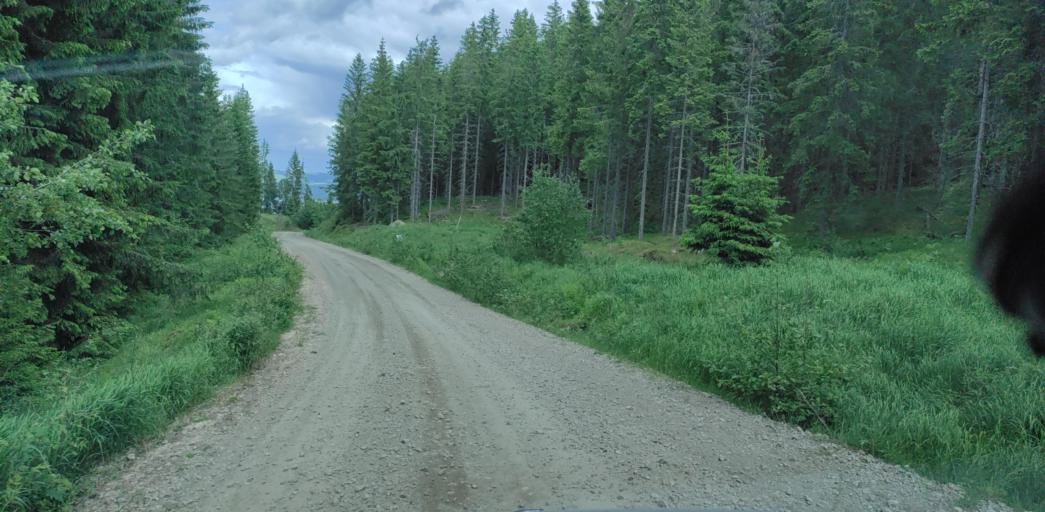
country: SE
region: Vaermland
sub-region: Munkfors Kommun
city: Munkfors
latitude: 59.9617
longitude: 13.4167
